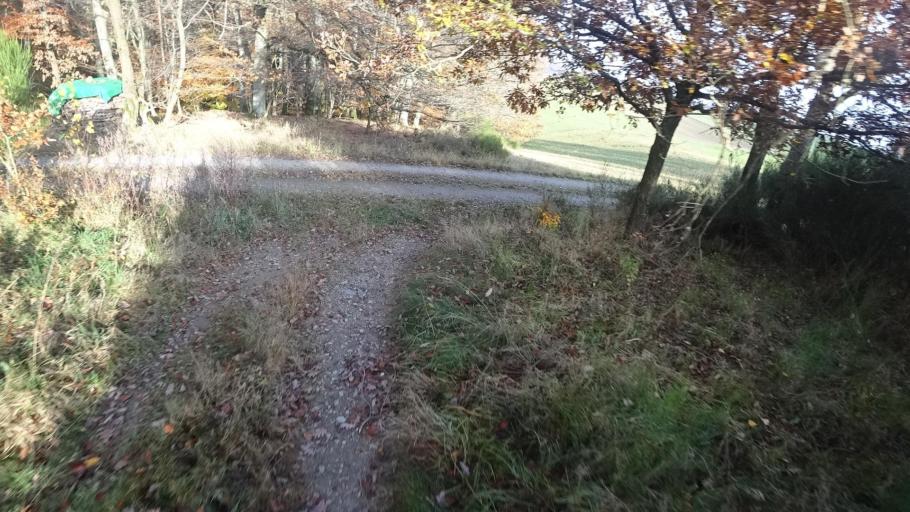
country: DE
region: Rheinland-Pfalz
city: Birkheim
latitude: 50.1301
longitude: 7.6191
